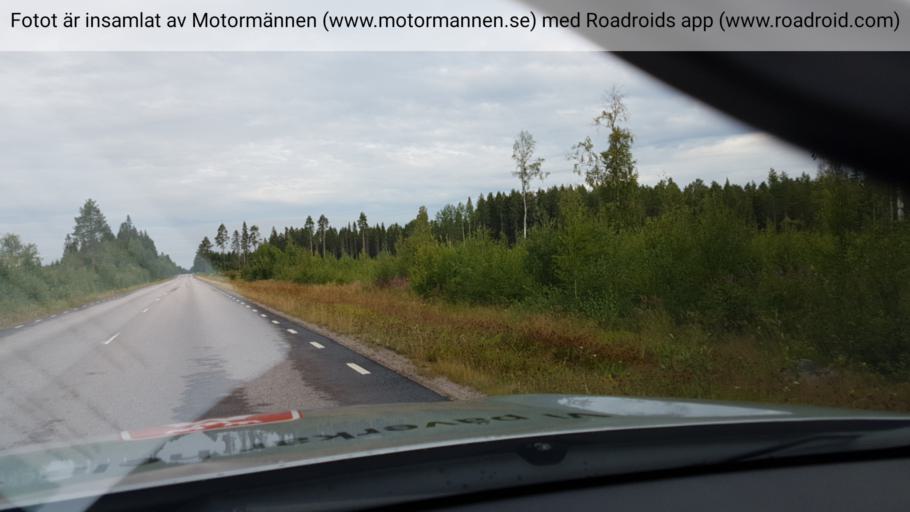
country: SE
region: Norrbotten
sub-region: Lulea Kommun
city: Sodra Sunderbyn
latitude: 65.6144
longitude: 21.9511
